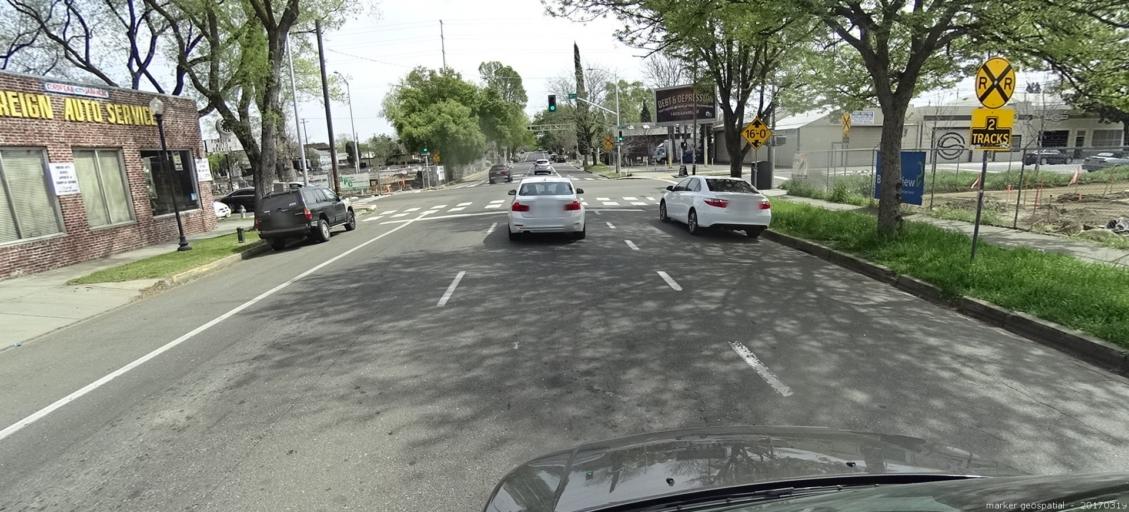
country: US
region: California
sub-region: Sacramento County
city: Sacramento
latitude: 38.5694
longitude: -121.4850
